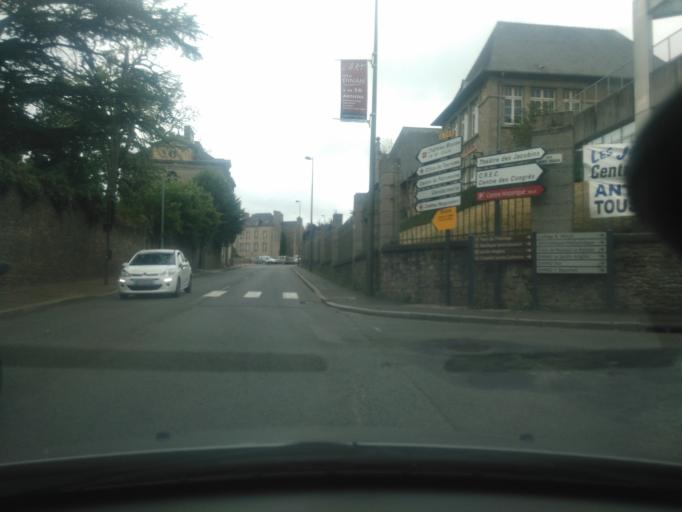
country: FR
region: Brittany
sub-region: Departement des Cotes-d'Armor
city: Lehon
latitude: 48.4508
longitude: -2.0416
